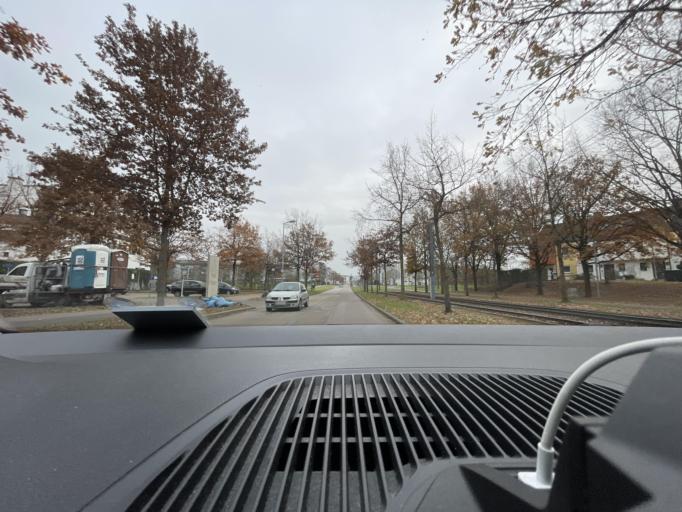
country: DE
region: Baden-Wuerttemberg
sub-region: Karlsruhe Region
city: Karlsruhe
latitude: 48.9844
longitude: 8.3630
